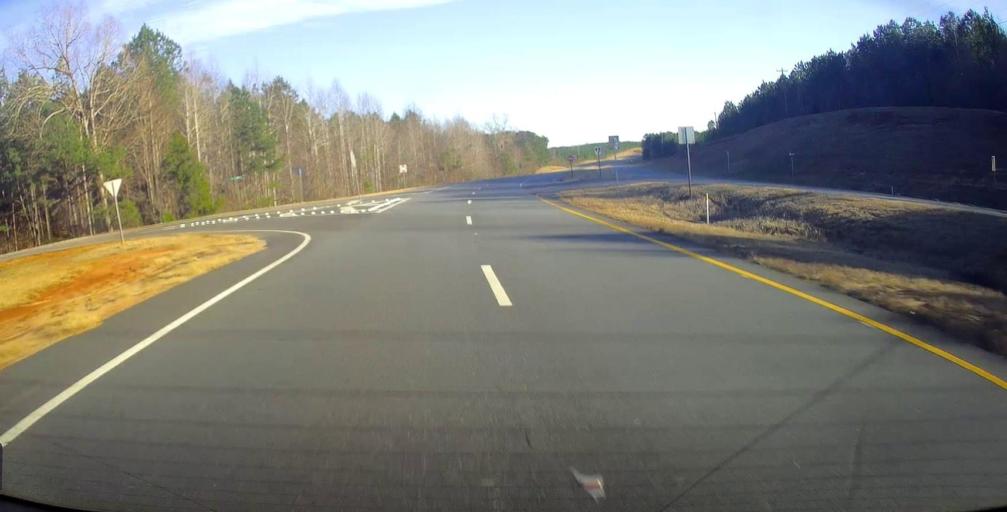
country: US
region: Georgia
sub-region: Upson County
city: Thomaston
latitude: 32.7889
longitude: -84.2491
